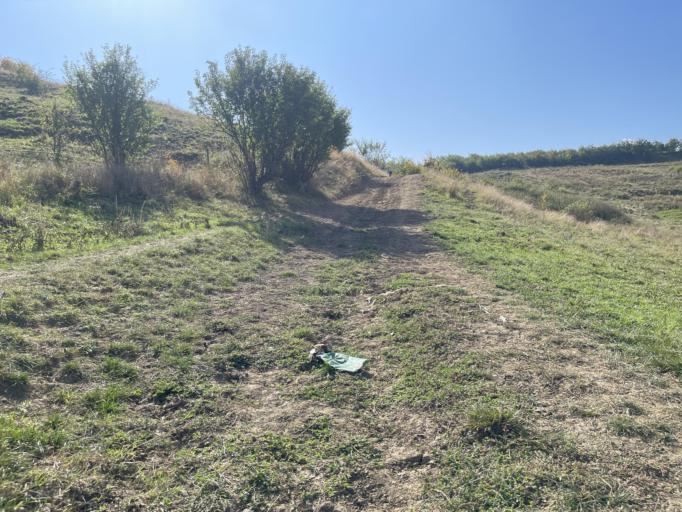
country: RO
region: Iasi
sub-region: Comuna Dumesti
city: Pausesti
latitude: 47.1596
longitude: 27.3143
